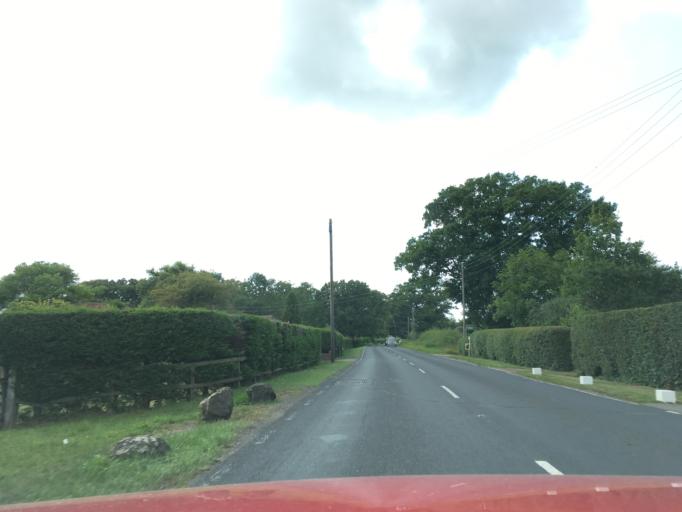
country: GB
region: England
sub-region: Kent
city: Tenterden
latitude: 51.1027
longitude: 0.6594
